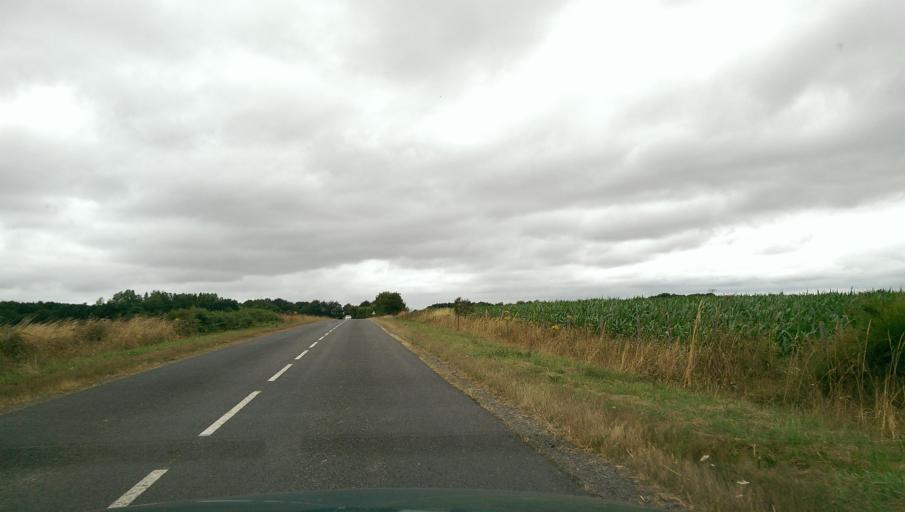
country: FR
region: Pays de la Loire
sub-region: Departement de la Loire-Atlantique
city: La Planche
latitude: 46.9954
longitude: -1.3853
